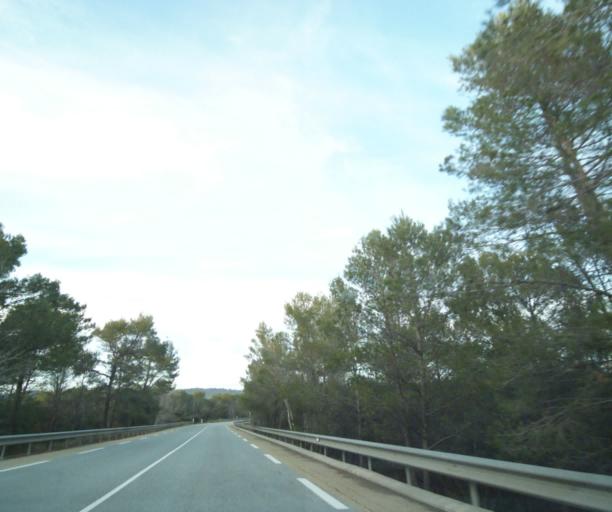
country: FR
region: Provence-Alpes-Cote d'Azur
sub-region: Departement du Var
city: La Motte
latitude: 43.5148
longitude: 6.5168
